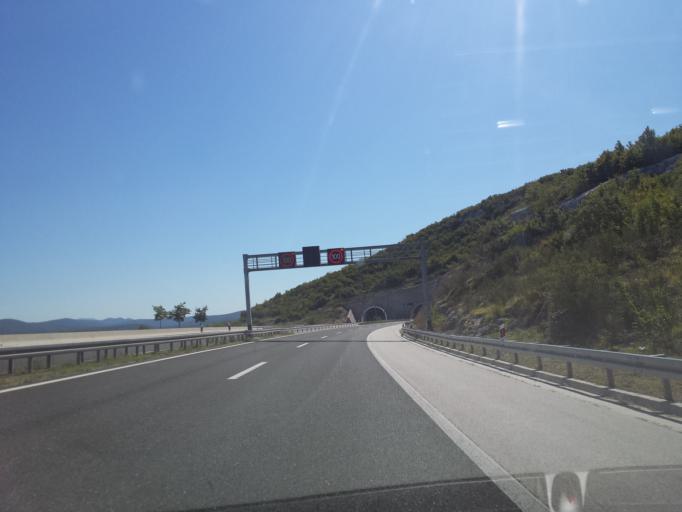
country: HR
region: Splitsko-Dalmatinska
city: Greda
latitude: 43.5816
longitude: 16.6602
